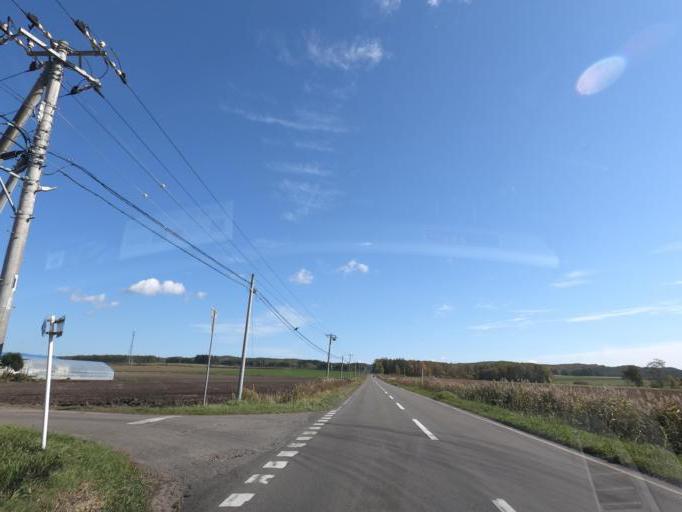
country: JP
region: Hokkaido
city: Otofuke
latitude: 43.0424
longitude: 143.2729
